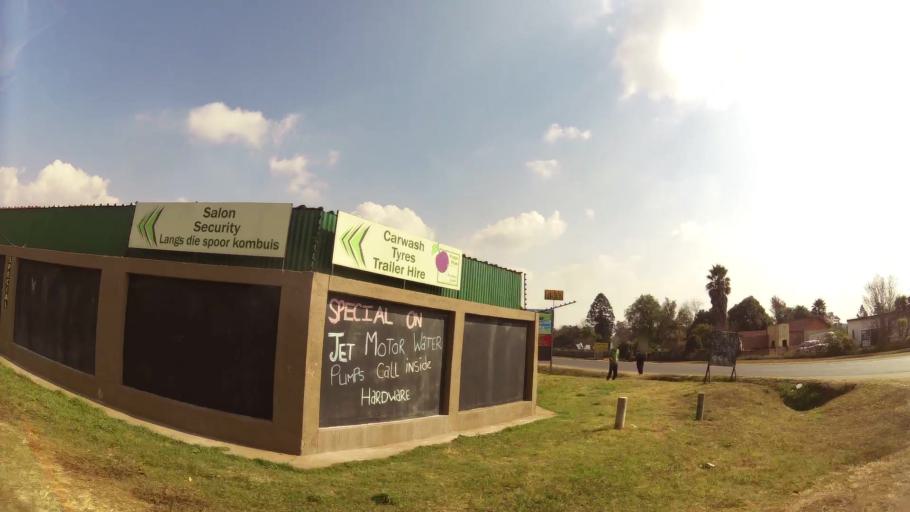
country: ZA
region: Mpumalanga
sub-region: Nkangala District Municipality
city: Delmas
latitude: -26.1873
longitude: 28.5401
